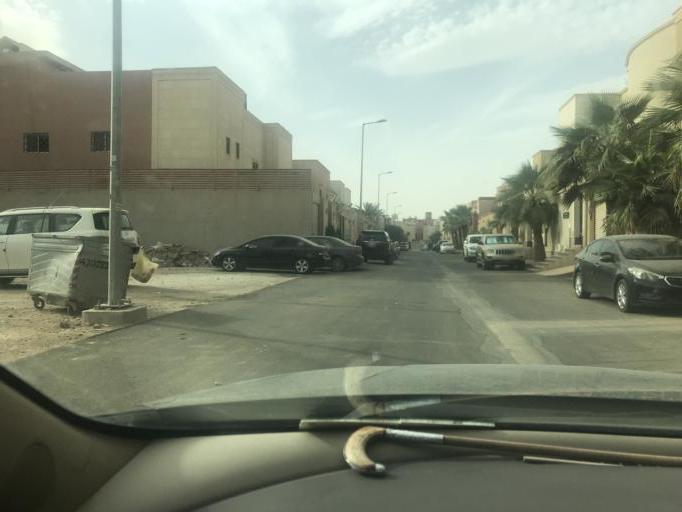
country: SA
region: Ar Riyad
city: Riyadh
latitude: 24.7985
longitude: 46.6699
